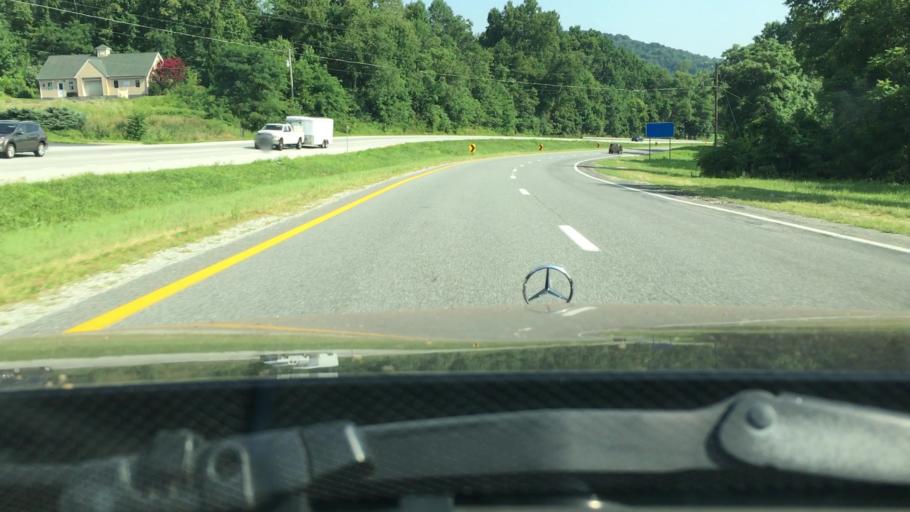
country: US
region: Virginia
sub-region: Nelson County
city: Lovingston
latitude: 37.7694
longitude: -78.8699
